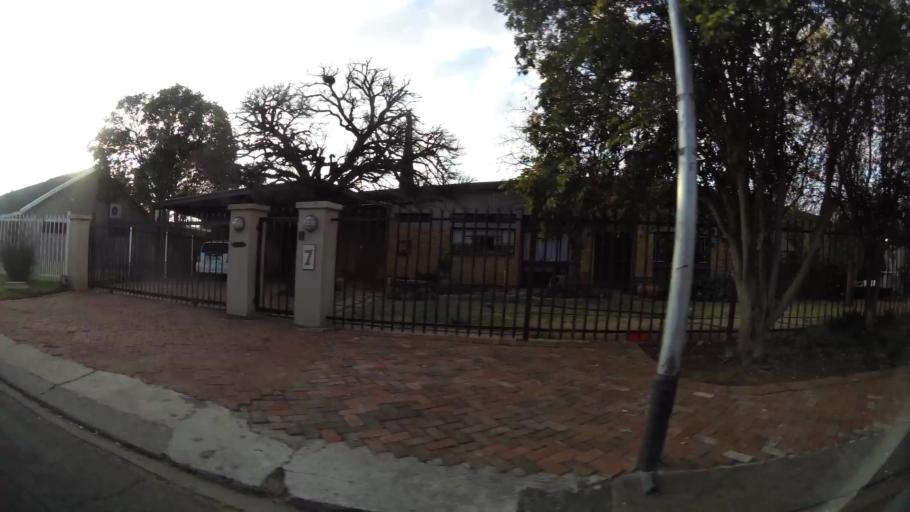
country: ZA
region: Orange Free State
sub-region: Mangaung Metropolitan Municipality
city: Bloemfontein
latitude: -29.1384
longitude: 26.1767
